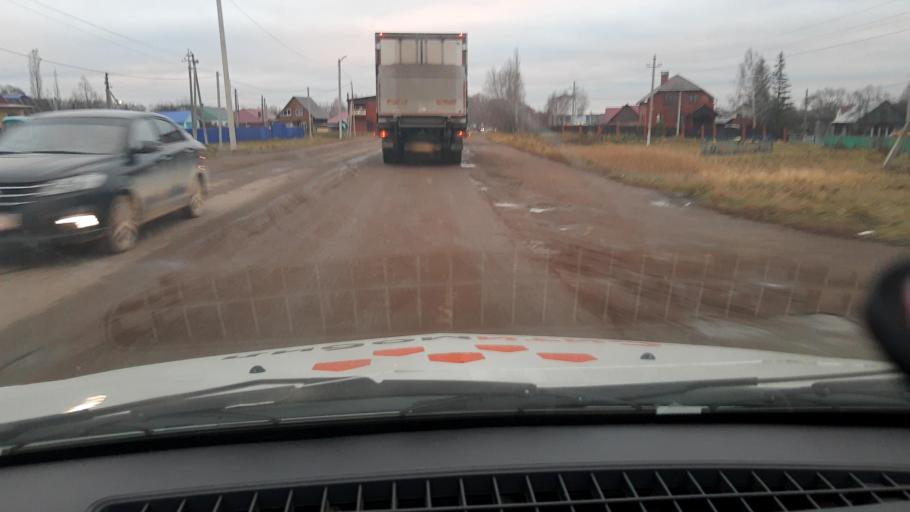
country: RU
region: Bashkortostan
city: Iglino
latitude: 54.8142
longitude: 56.4067
